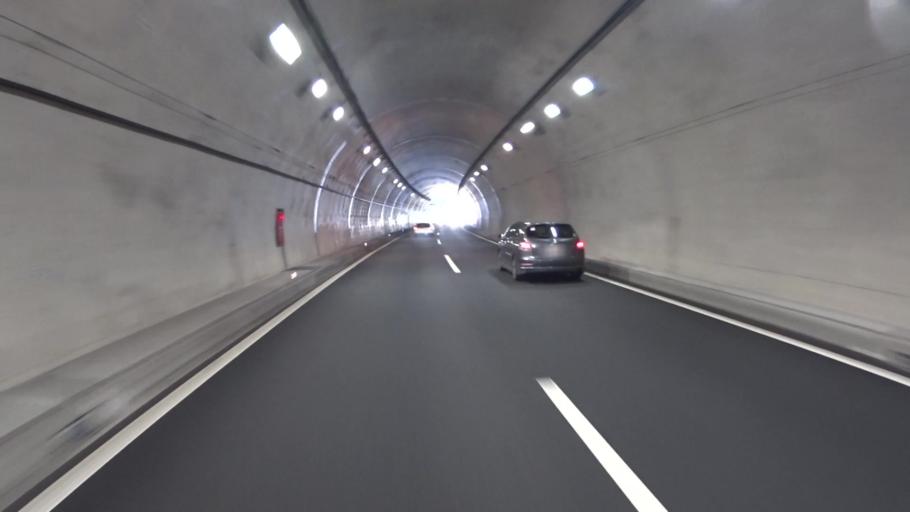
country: JP
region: Kyoto
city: Muko
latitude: 34.9607
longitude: 135.6535
